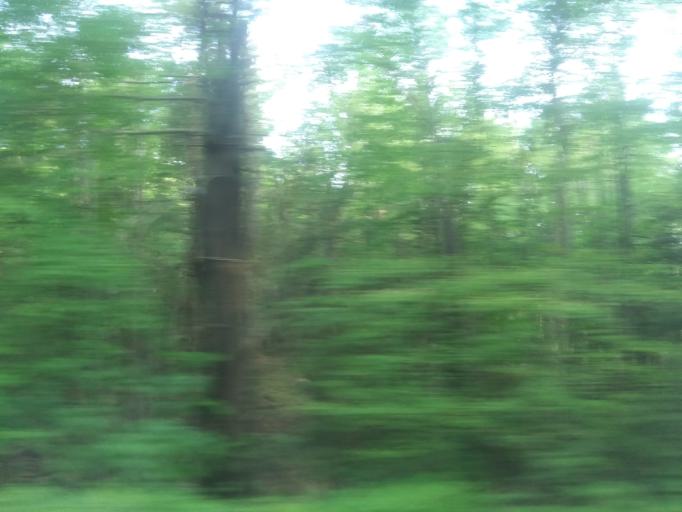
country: US
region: Massachusetts
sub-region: Franklin County
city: Shelburne Falls
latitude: 42.5770
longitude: -72.7593
